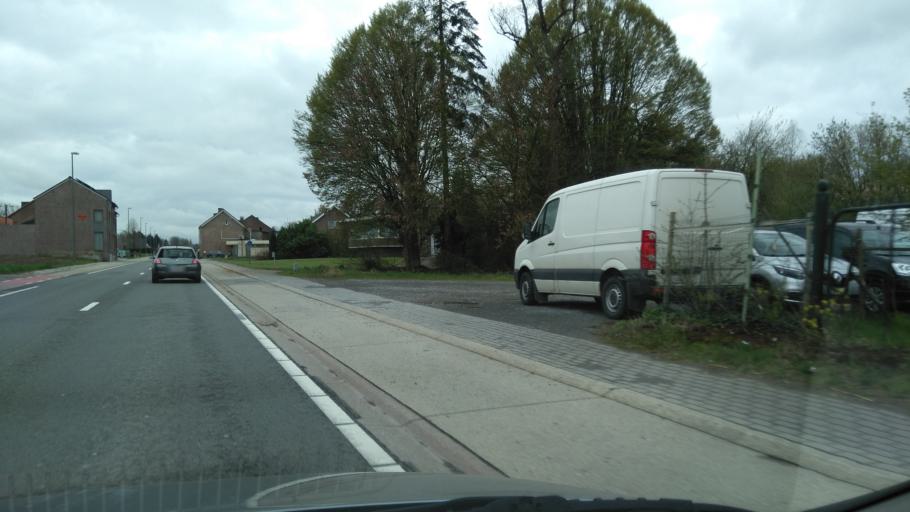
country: BE
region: Flanders
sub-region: Provincie Limburg
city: Bilzen
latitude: 50.8515
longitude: 5.5379
